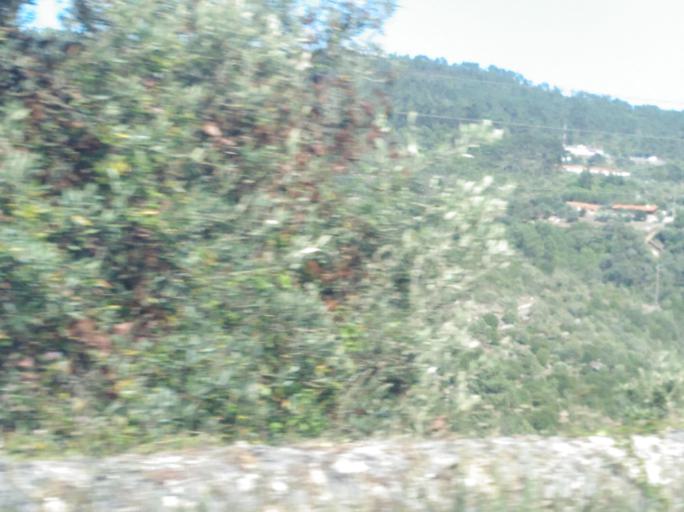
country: PT
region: Leiria
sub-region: Porto de Mos
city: Porto de Mos
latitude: 39.5799
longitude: -8.8048
